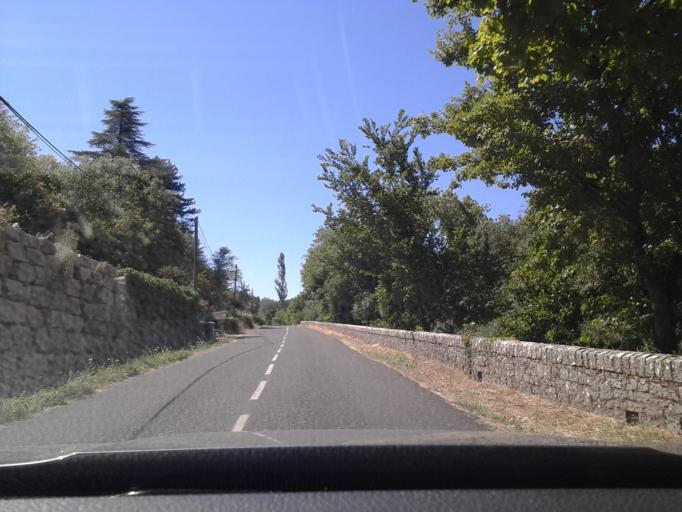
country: FR
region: Languedoc-Roussillon
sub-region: Departement de l'Herault
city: Montpeyroux
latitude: 43.7870
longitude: 3.4623
